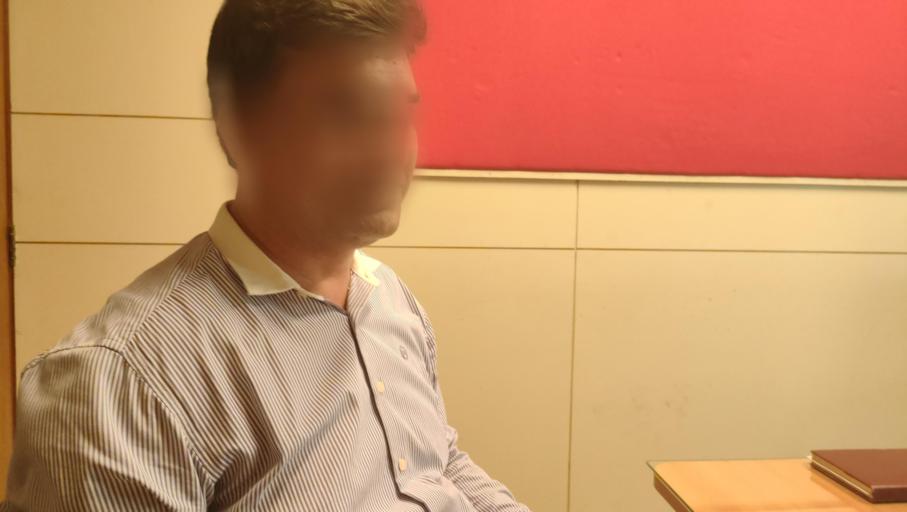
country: PK
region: Sindh
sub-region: Karachi District
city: Karachi
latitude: 24.8208
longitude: 67.0714
